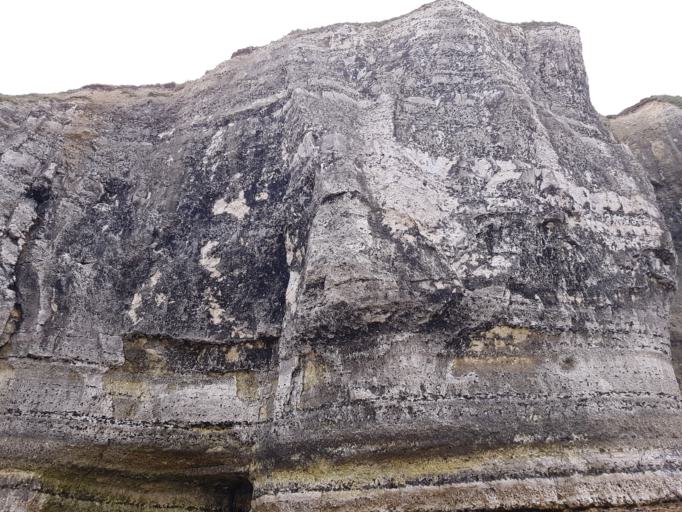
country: FR
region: Haute-Normandie
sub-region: Departement de la Seine-Maritime
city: Etretat
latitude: 49.7067
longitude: 0.1975
